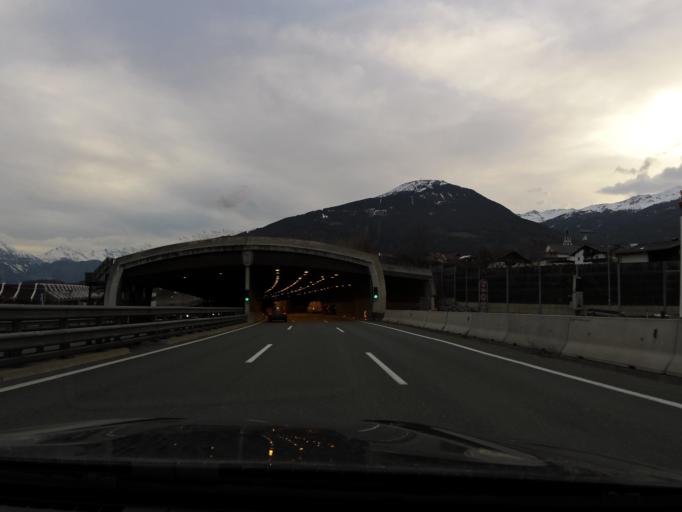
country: AT
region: Tyrol
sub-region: Politischer Bezirk Innsbruck Land
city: Schoenberg im Stubaital
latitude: 47.1850
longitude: 11.3988
